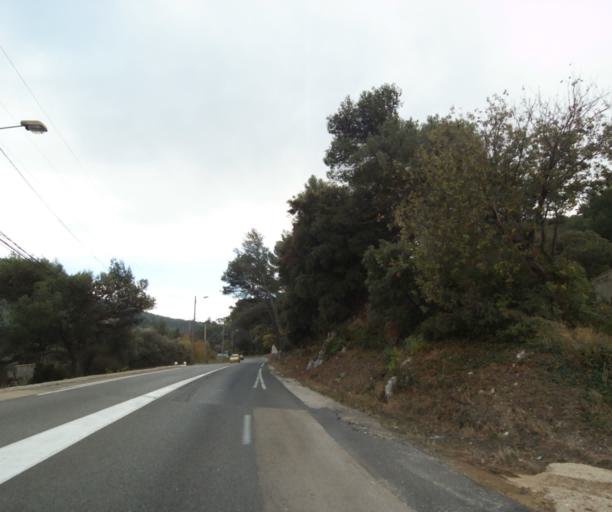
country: FR
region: Provence-Alpes-Cote d'Azur
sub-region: Departement des Bouches-du-Rhone
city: Gemenos
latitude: 43.2736
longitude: 5.6383
